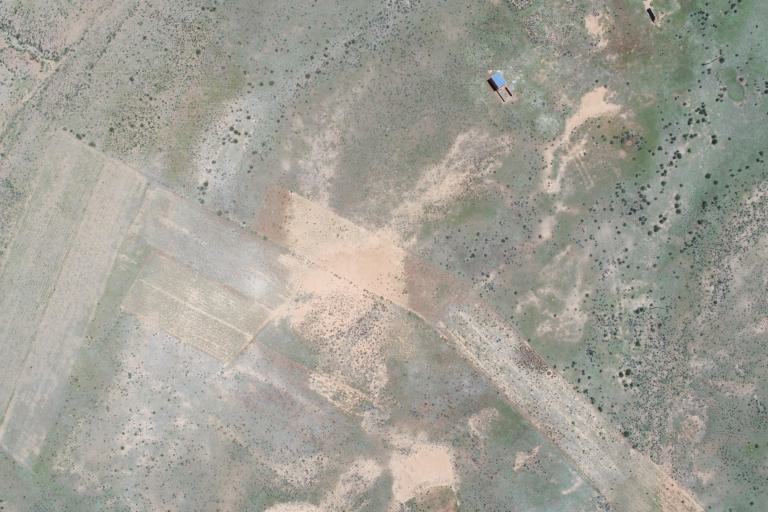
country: BO
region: La Paz
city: Patacamaya
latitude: -17.2740
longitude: -68.5167
